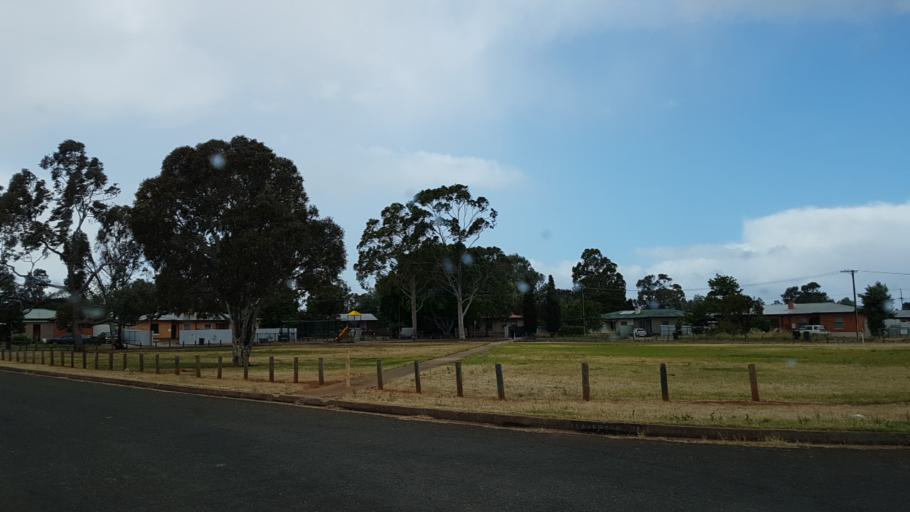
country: AU
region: South Australia
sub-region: Playford
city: Smithfield
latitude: -34.6931
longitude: 138.6643
